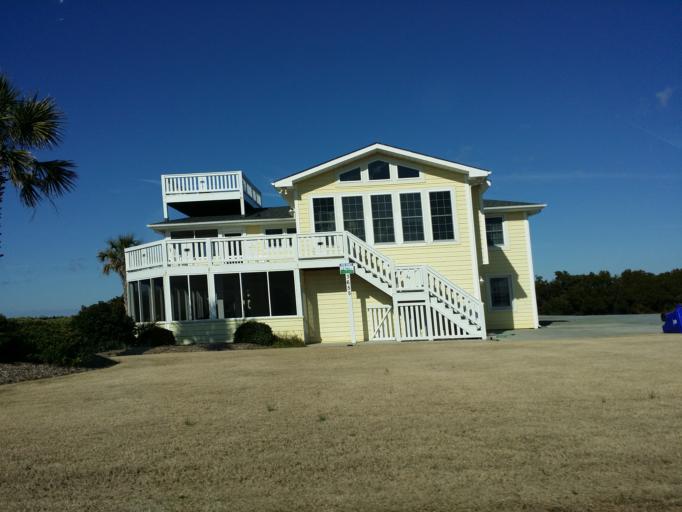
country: US
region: North Carolina
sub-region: Onslow County
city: Holly Ridge
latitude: 34.4740
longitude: -77.4607
